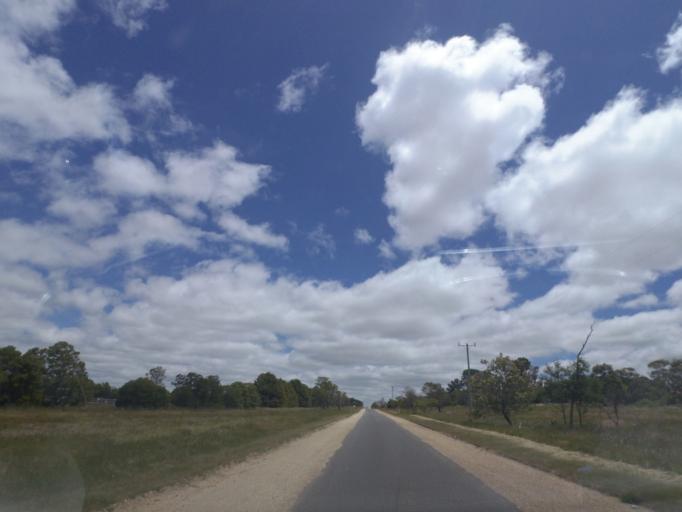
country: AU
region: Victoria
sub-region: Moorabool
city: Bacchus Marsh
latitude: -37.6375
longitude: 144.2779
